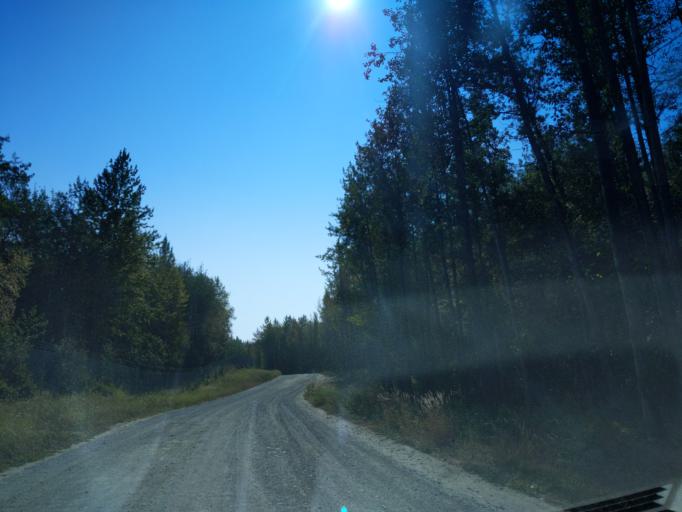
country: US
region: Alaska
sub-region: Anchorage Municipality
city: Anchorage
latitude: 61.1623
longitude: -150.0143
